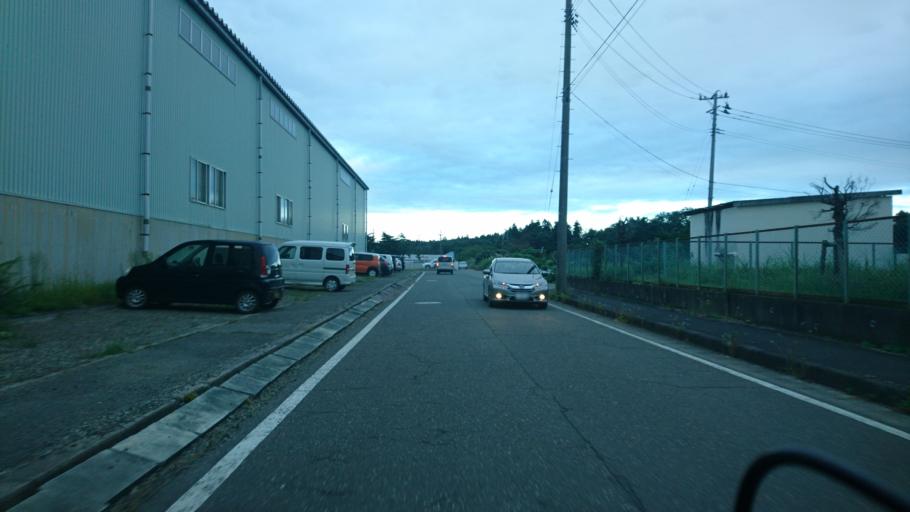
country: JP
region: Iwate
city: Kitakami
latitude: 39.3127
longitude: 141.0979
